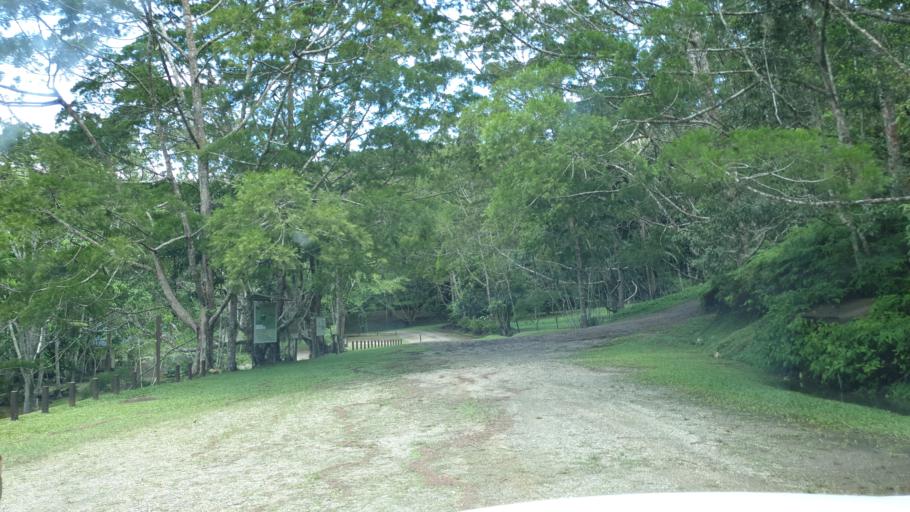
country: PG
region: National Capital
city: Port Moresby
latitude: -9.4361
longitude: 147.3639
